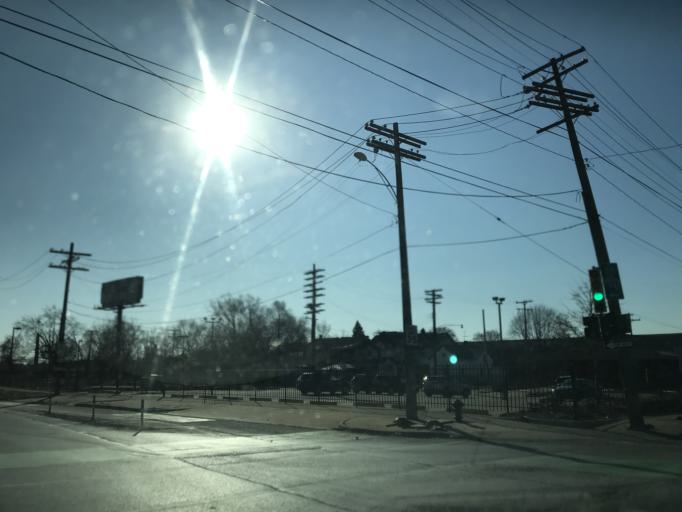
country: US
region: Michigan
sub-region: Wayne County
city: Grosse Pointe Park
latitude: 42.3972
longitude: -82.9900
